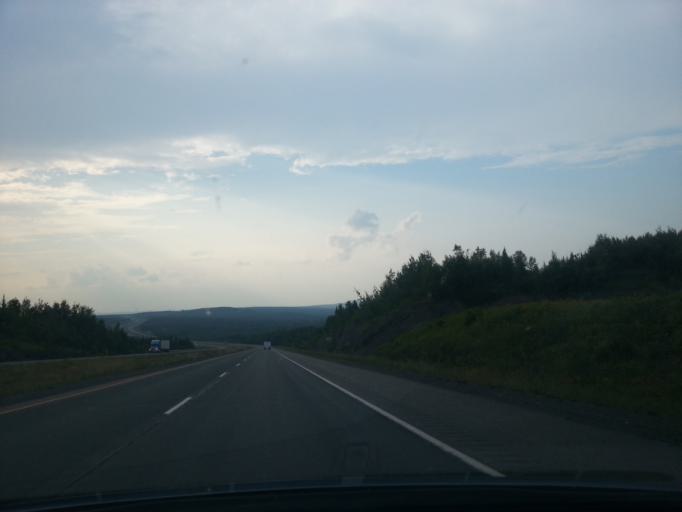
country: CA
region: New Brunswick
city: Harrison Brook
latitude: 47.2815
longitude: -68.0248
